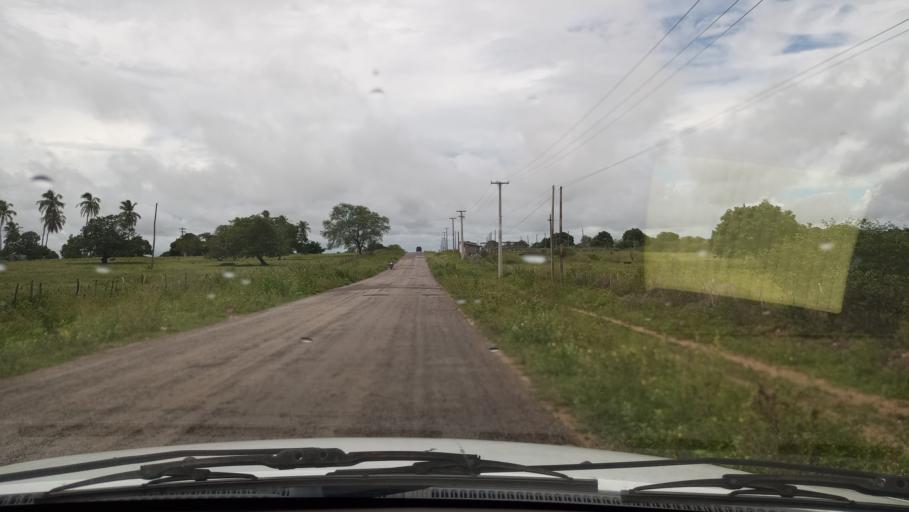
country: BR
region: Rio Grande do Norte
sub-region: Poco Branco
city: Poco Branco
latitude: -5.6147
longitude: -35.6488
